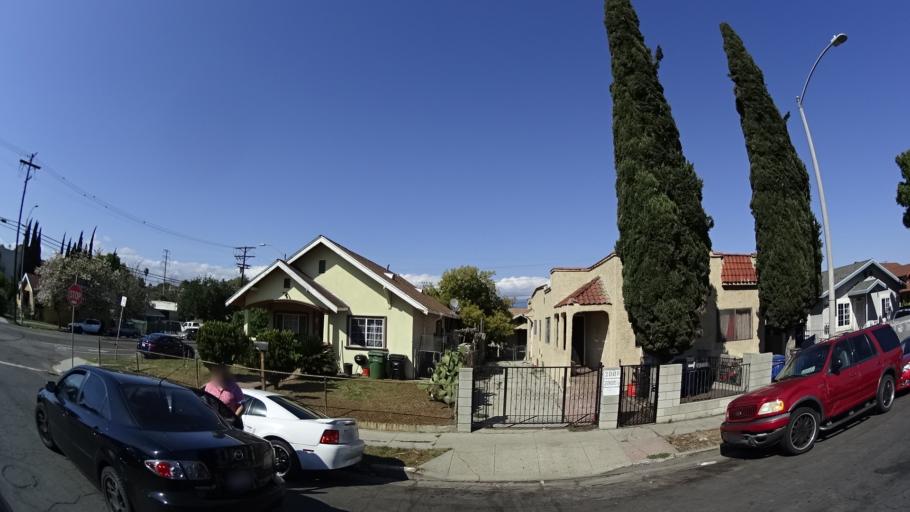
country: US
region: California
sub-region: Los Angeles County
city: Boyle Heights
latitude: 34.0496
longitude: -118.1983
